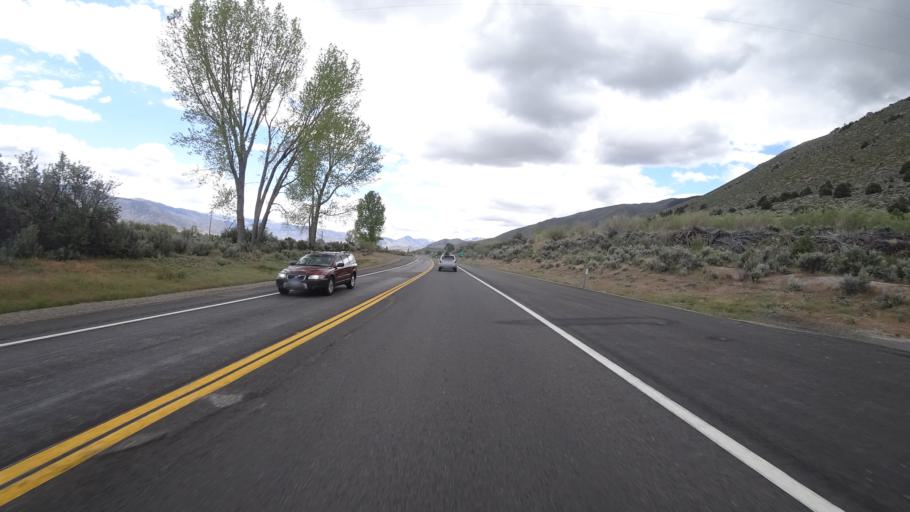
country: US
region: Nevada
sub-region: Lyon County
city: Smith Valley
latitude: 38.6084
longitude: -119.5201
